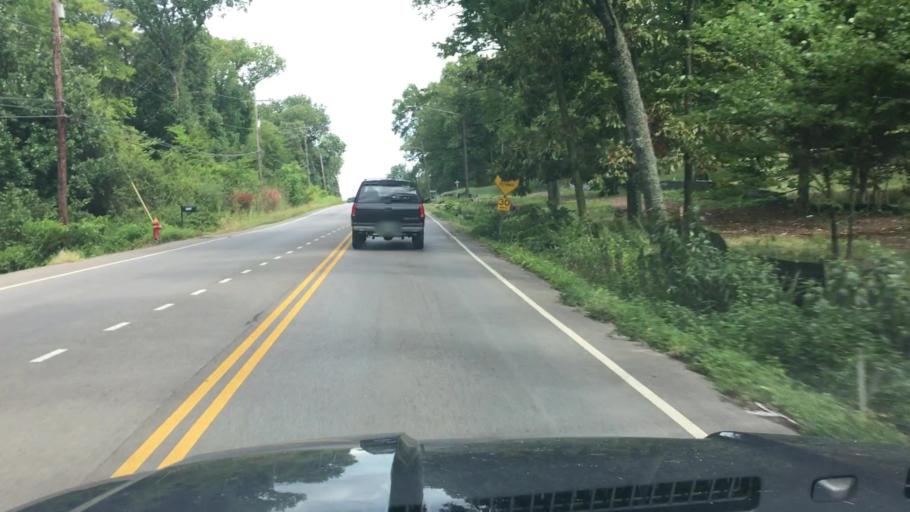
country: US
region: Tennessee
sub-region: Davidson County
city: Oak Hill
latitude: 36.0902
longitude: -86.8117
